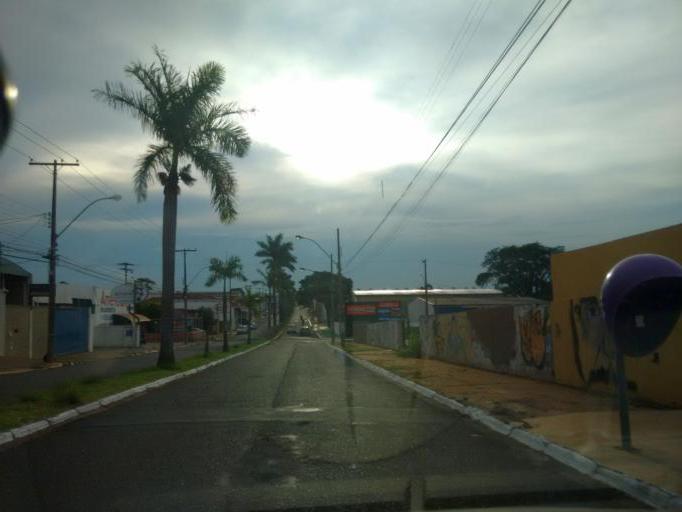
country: BR
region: Sao Paulo
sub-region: Araraquara
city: Araraquara
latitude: -21.8028
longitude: -48.1936
